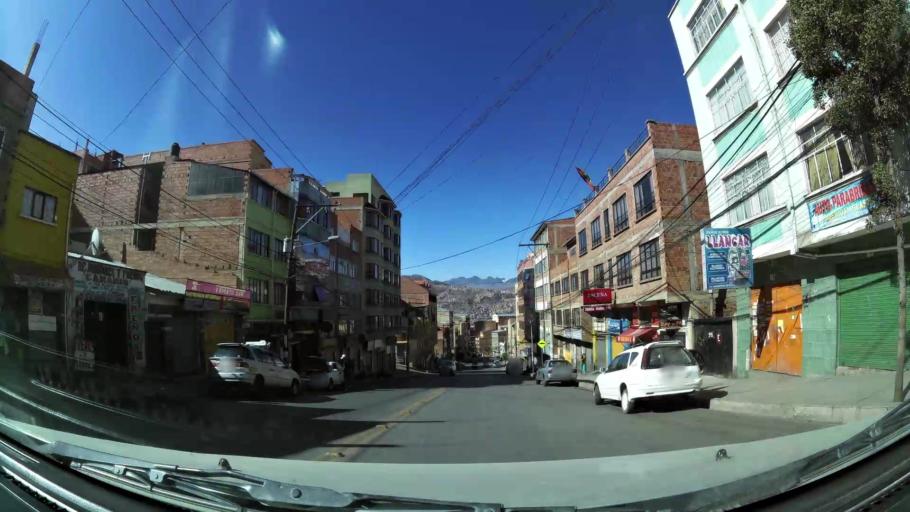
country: BO
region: La Paz
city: La Paz
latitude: -16.5112
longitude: -68.1386
